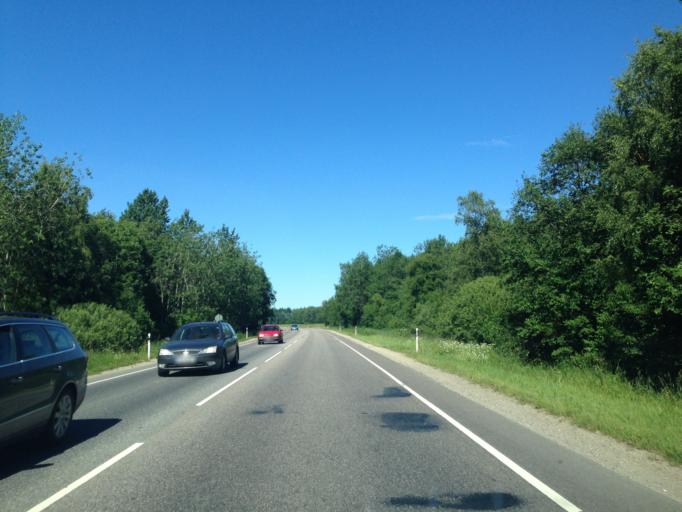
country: EE
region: Harju
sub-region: Rae vald
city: Jueri
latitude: 59.3770
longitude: 24.9146
